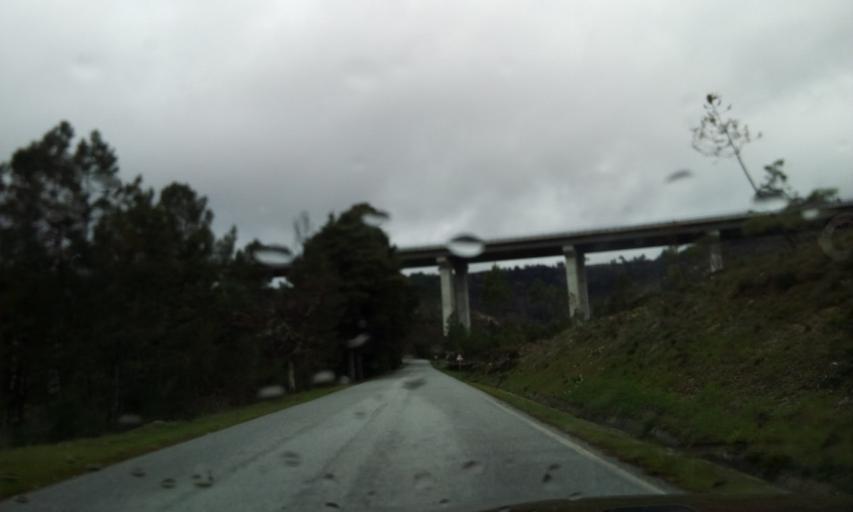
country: PT
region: Guarda
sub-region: Fornos de Algodres
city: Fornos de Algodres
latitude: 40.6228
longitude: -7.5881
